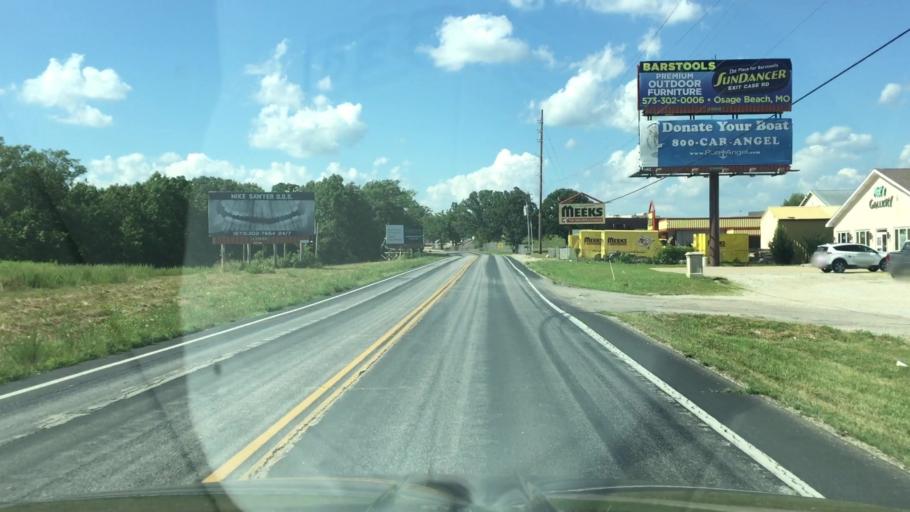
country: US
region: Missouri
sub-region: Camden County
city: Osage Beach
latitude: 38.1427
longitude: -92.5914
